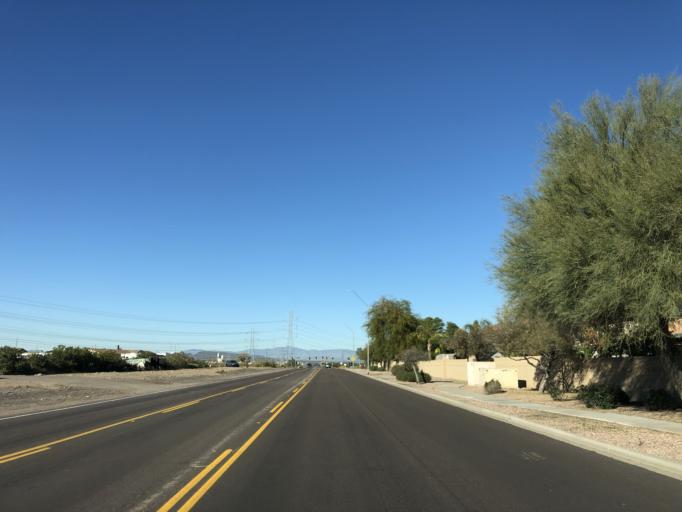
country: US
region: Arizona
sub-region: Maricopa County
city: Sun City West
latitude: 33.6930
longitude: -112.2897
